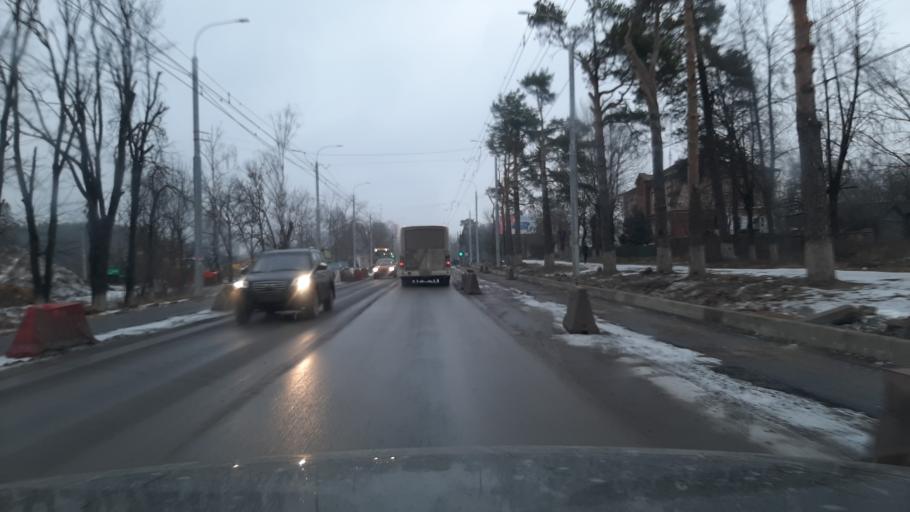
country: RU
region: Ivanovo
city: Kokhma
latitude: 56.9369
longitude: 41.0685
